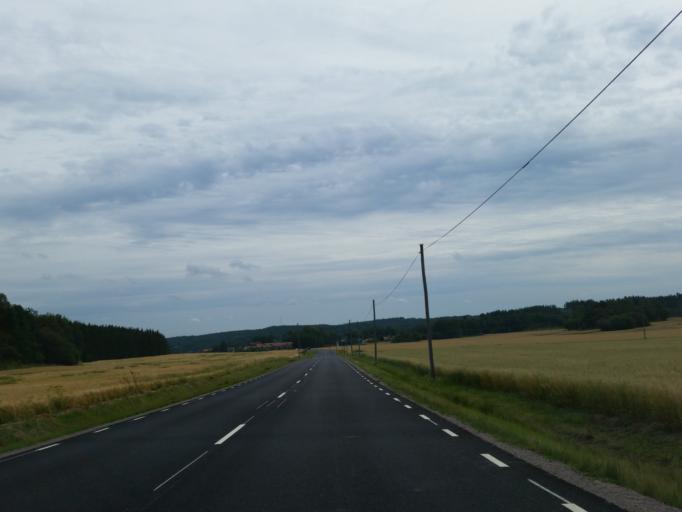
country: SE
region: Soedermanland
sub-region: Strangnas Kommun
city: Mariefred
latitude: 59.2600
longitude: 17.1695
